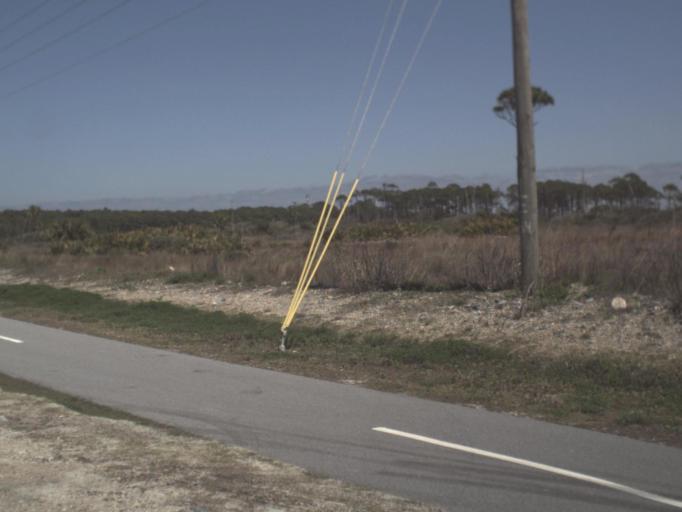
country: US
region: Florida
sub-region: Gulf County
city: Port Saint Joe
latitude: 29.6787
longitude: -85.3654
